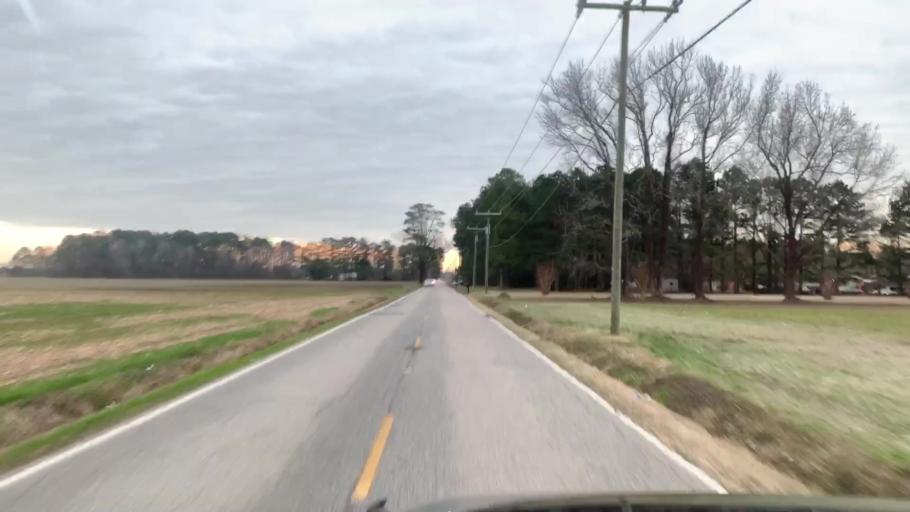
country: US
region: North Carolina
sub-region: Currituck County
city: Moyock
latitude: 36.6326
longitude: -76.1819
